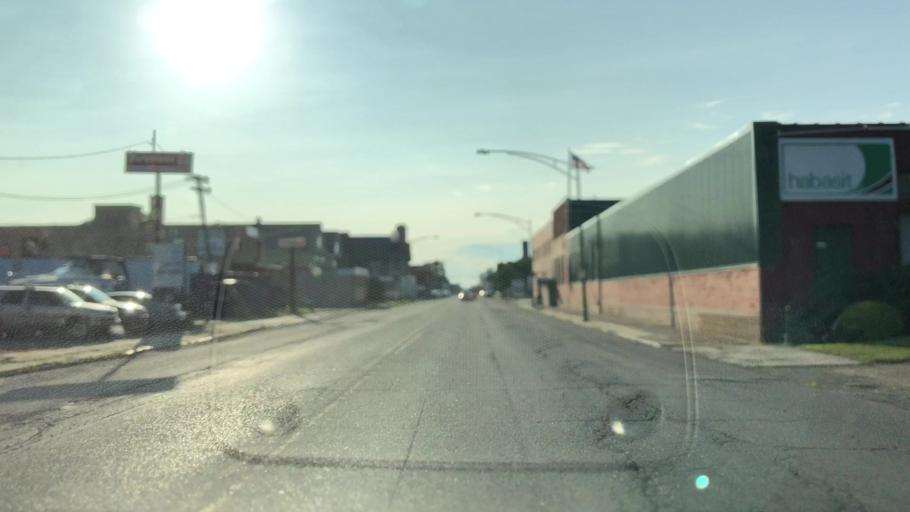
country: US
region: New York
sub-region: Erie County
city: West Seneca
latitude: 42.8735
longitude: -78.8237
